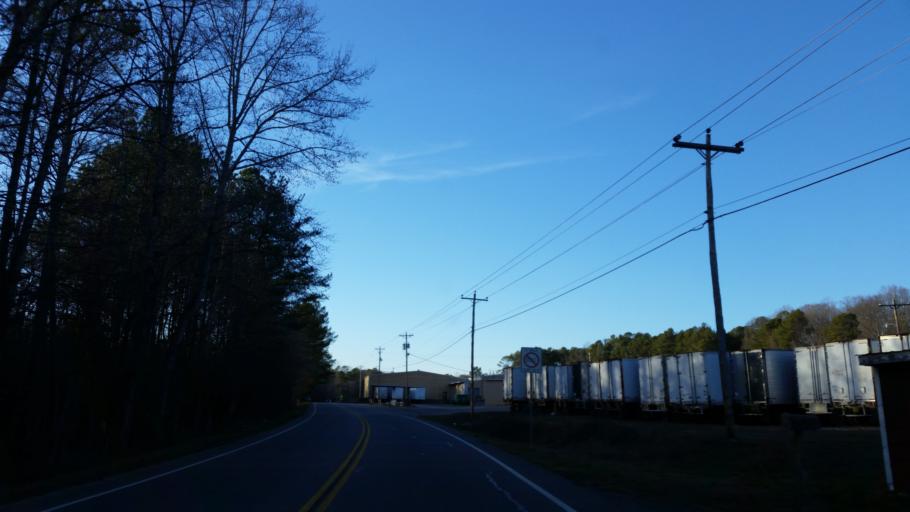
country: US
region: Georgia
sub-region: Gordon County
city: Calhoun
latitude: 34.6239
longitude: -84.9510
